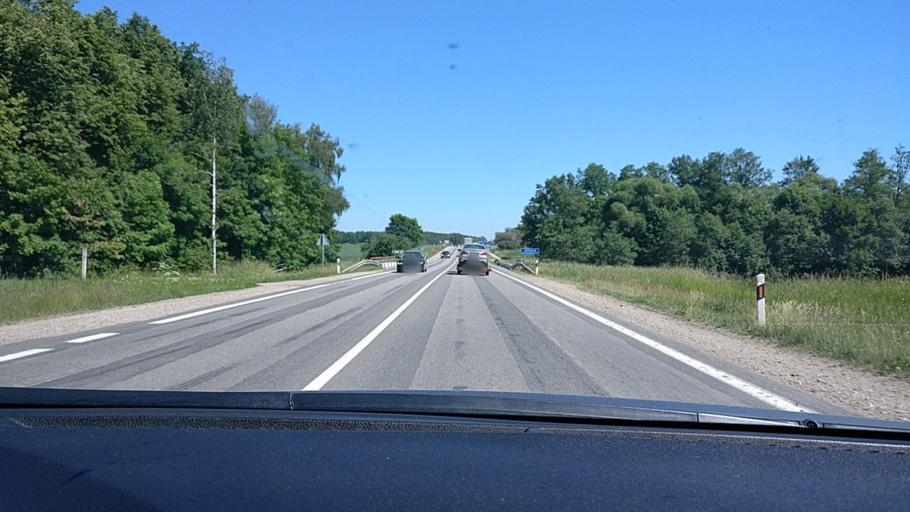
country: LT
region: Panevezys
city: Pasvalys
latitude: 56.1078
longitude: 24.4640
